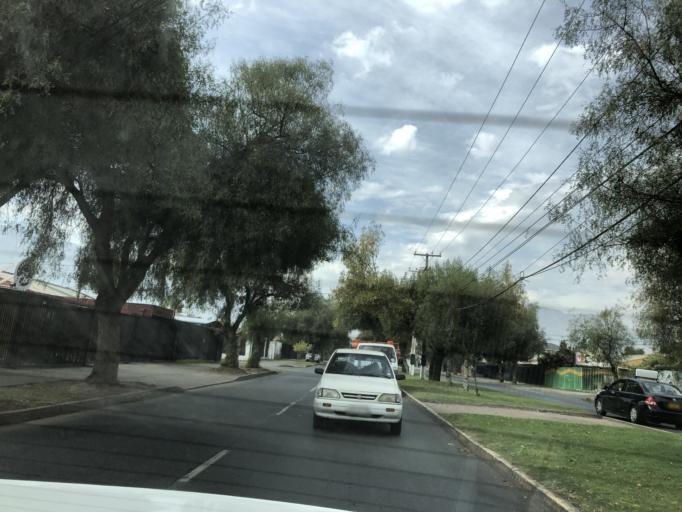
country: CL
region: Santiago Metropolitan
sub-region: Provincia de Cordillera
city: Puente Alto
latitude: -33.5974
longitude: -70.5717
